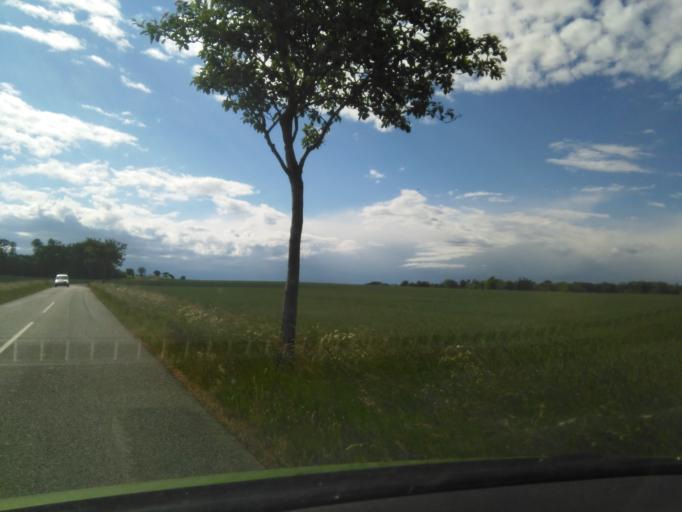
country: DK
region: Capital Region
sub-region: Bornholm Kommune
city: Nexo
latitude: 55.1242
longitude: 15.0684
